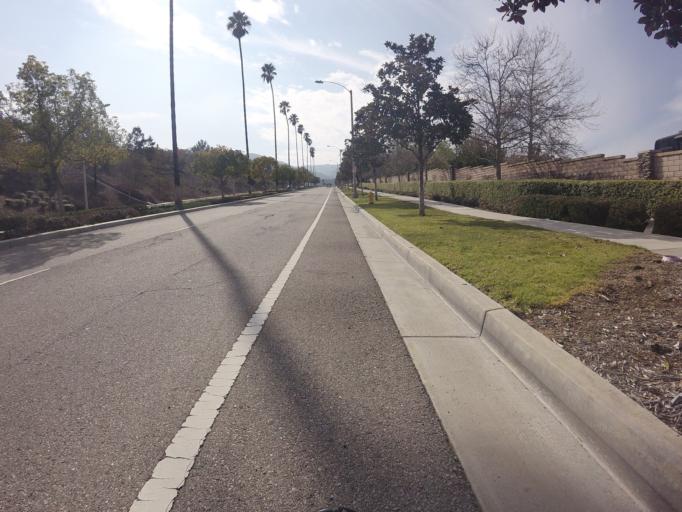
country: US
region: California
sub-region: Riverside County
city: Corona
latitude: 33.8436
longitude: -117.5896
